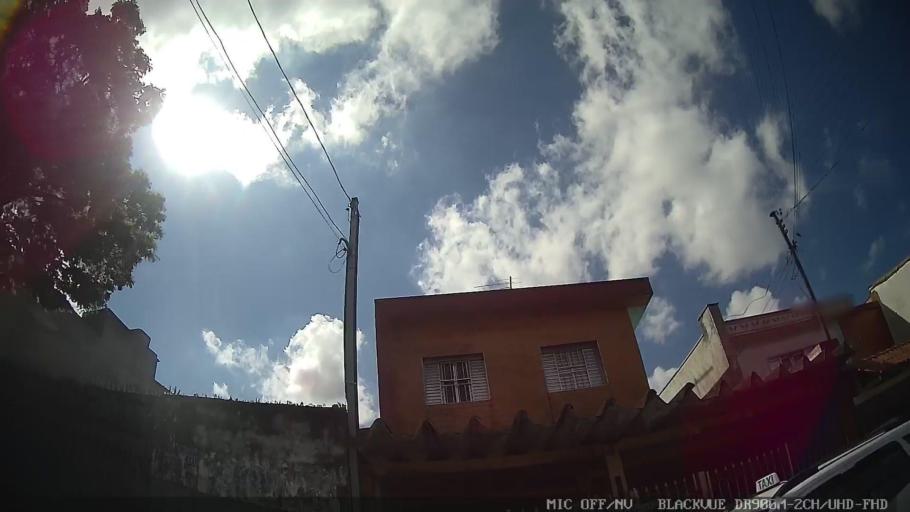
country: BR
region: Sao Paulo
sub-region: Sao Caetano Do Sul
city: Sao Caetano do Sul
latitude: -23.6217
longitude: -46.5885
